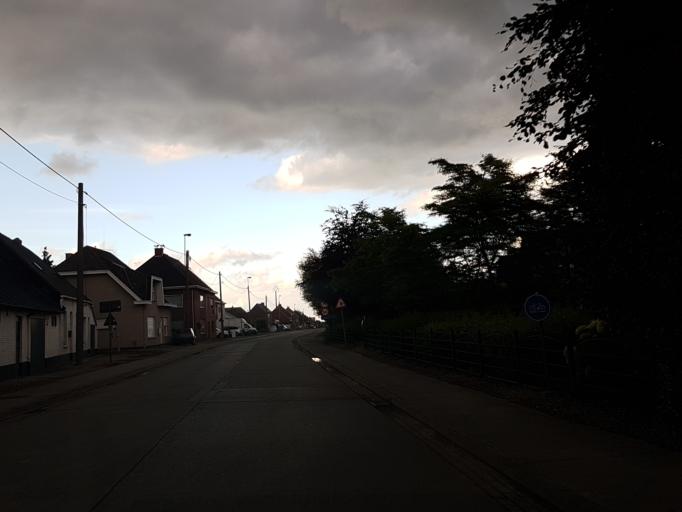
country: BE
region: Flanders
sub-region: Provincie Oost-Vlaanderen
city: Buggenhout
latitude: 50.9986
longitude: 4.1930
